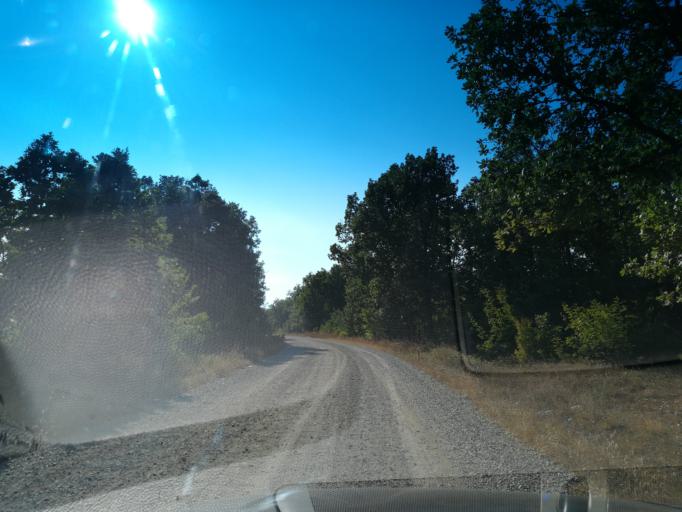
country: BG
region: Khaskovo
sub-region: Obshtina Mineralni Bani
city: Mineralni Bani
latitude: 41.9716
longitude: 25.3232
